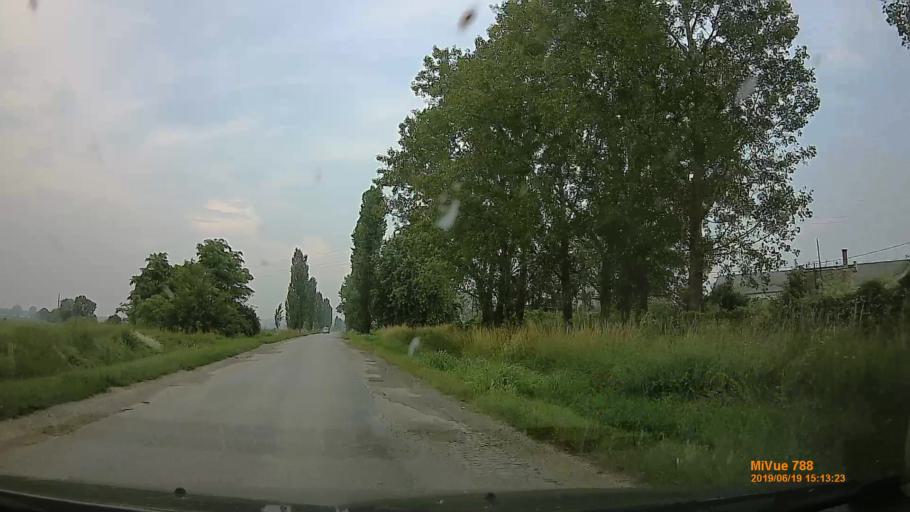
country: HU
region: Baranya
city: Szigetvar
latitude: 46.0604
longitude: 17.8150
